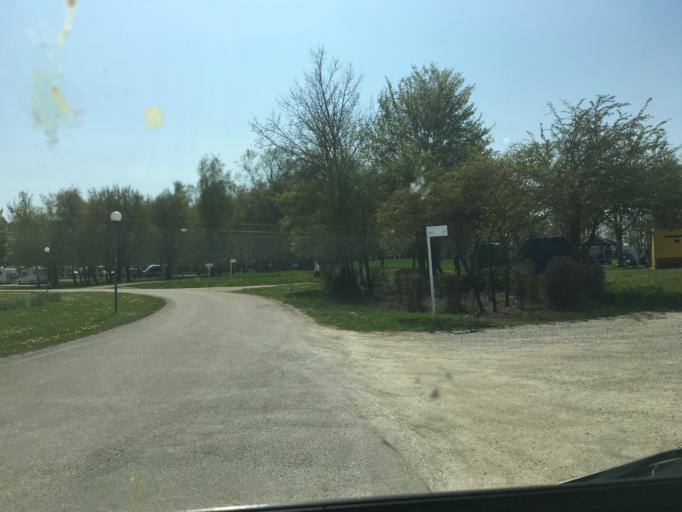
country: FR
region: Lorraine
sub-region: Departement de la Meuse
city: Vigneulles-les-Hattonchatel
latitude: 48.9375
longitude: 5.7133
